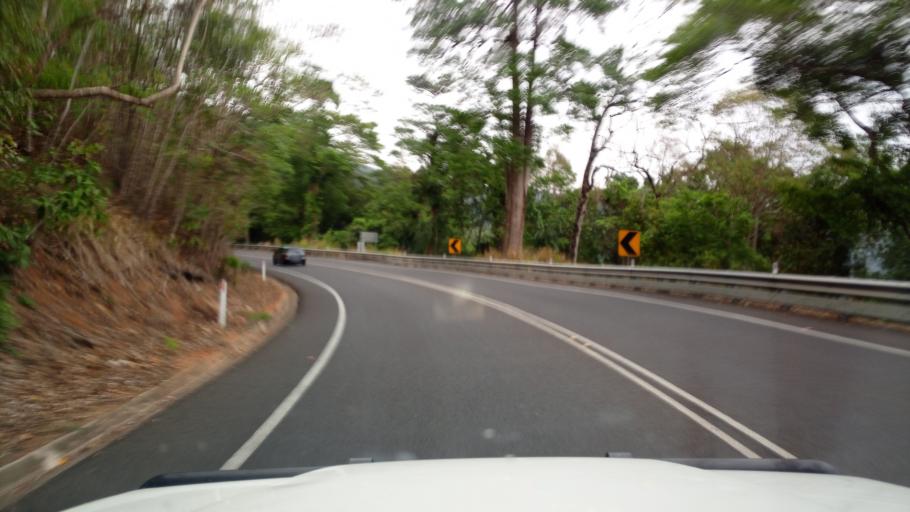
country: AU
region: Queensland
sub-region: Cairns
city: Redlynch
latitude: -16.8508
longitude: 145.6862
